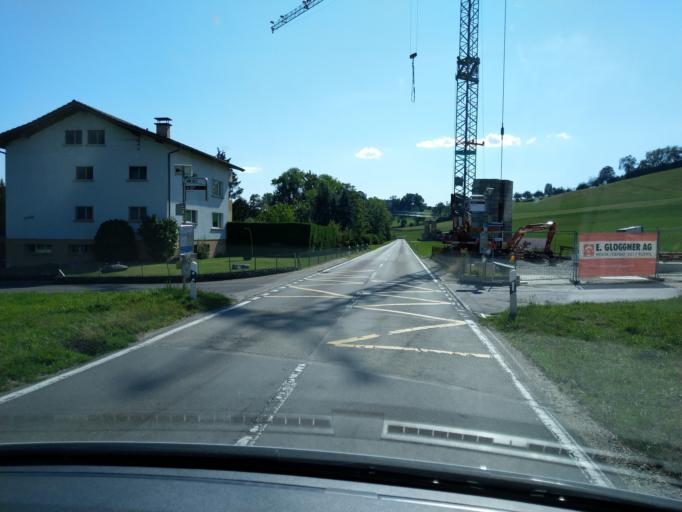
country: CH
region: Lucerne
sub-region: Entlebuch District
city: Werthenstein
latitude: 47.0705
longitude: 8.1030
